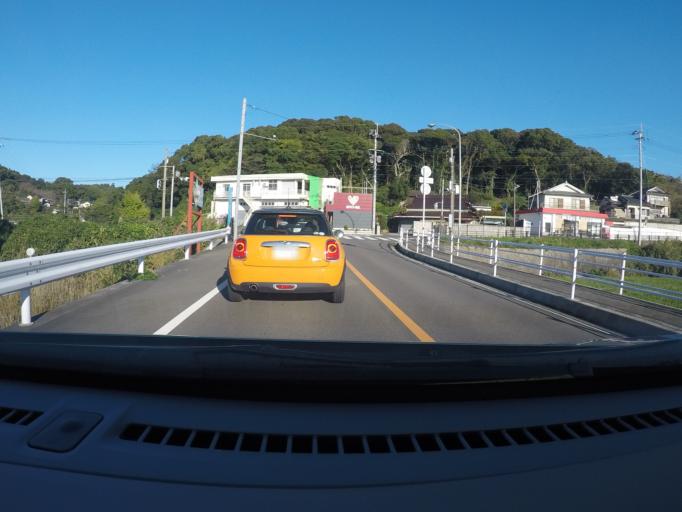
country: JP
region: Kumamoto
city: Minamata
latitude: 32.1791
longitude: 130.3826
